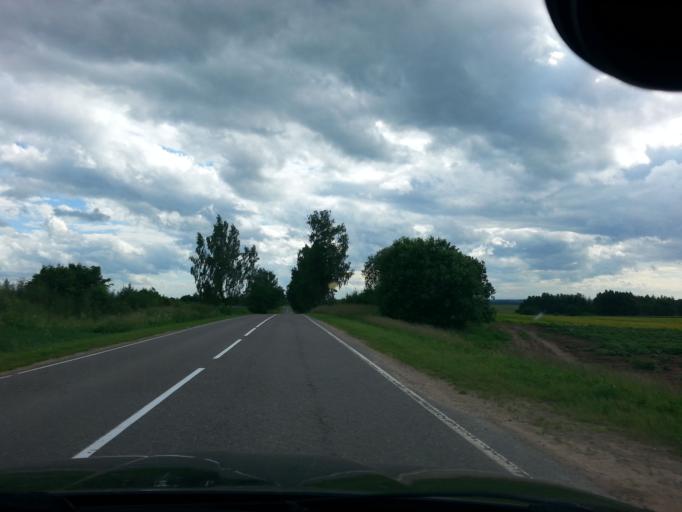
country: BY
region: Minsk
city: Svir
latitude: 54.9090
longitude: 26.3927
